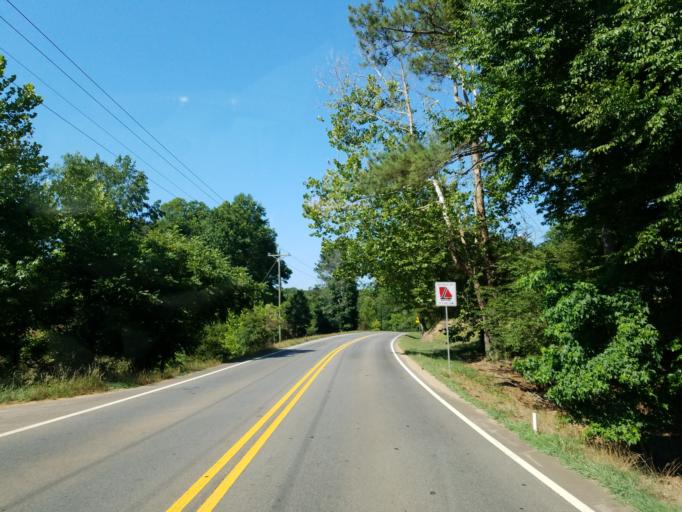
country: US
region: Georgia
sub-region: Fulton County
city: Milton
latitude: 34.1906
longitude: -84.3141
